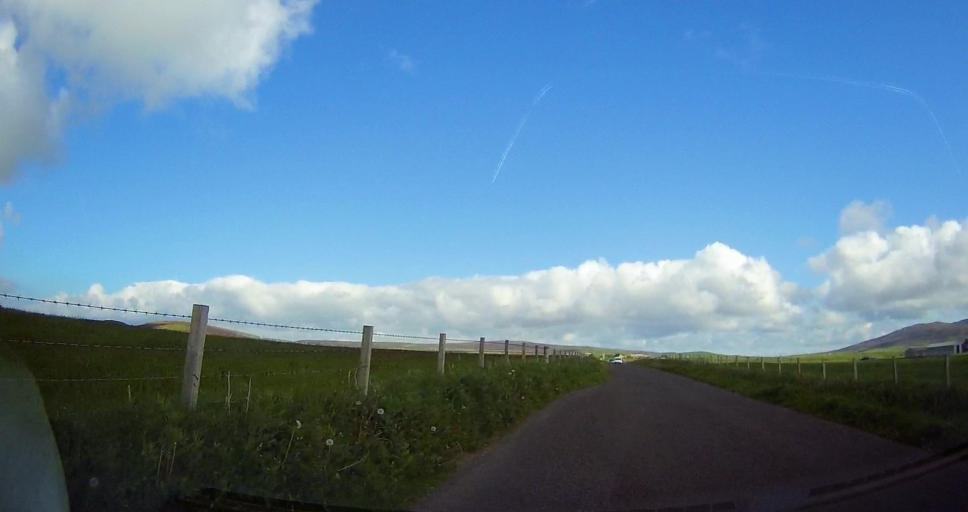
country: GB
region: Scotland
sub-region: Orkney Islands
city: Stromness
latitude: 58.9997
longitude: -3.1719
